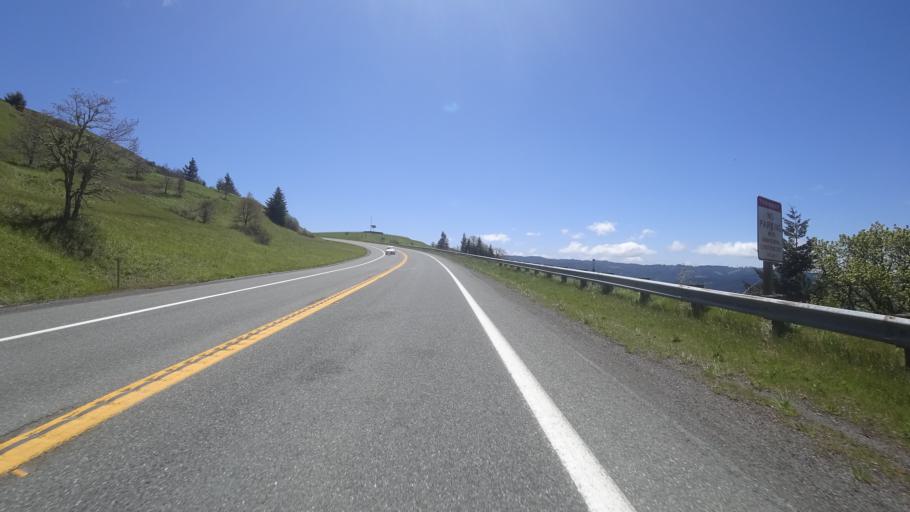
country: US
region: California
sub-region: Humboldt County
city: Willow Creek
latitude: 40.9042
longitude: -123.7812
